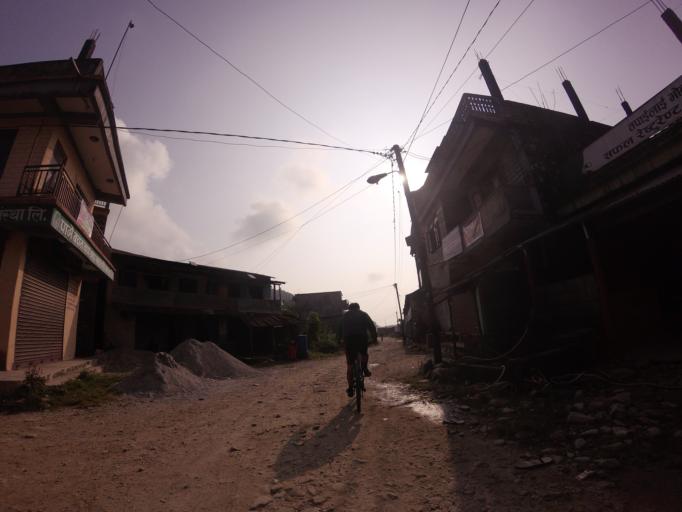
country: NP
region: Western Region
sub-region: Gandaki Zone
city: Pokhara
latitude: 28.2359
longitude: 83.9095
